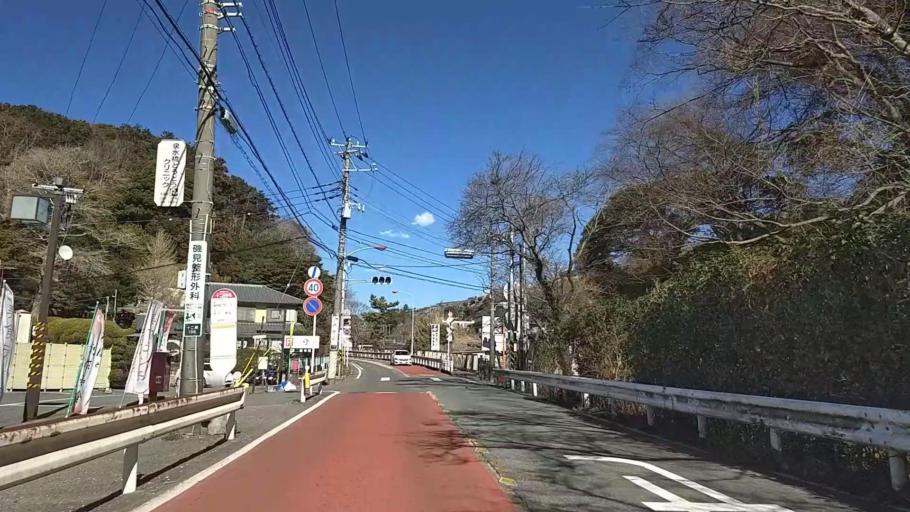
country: JP
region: Kanagawa
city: Zushi
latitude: 35.3228
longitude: 139.5810
